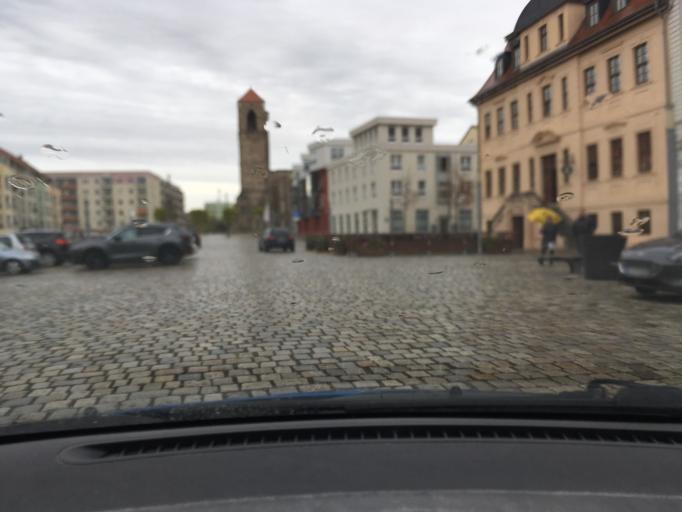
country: DE
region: Saxony-Anhalt
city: Zerbst
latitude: 51.9677
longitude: 12.0848
